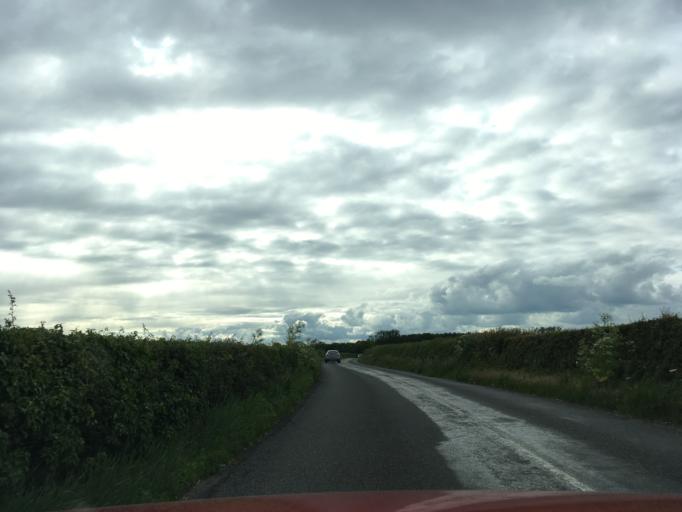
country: GB
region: England
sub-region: Oxfordshire
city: Boars Hill
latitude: 51.7114
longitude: -1.3262
